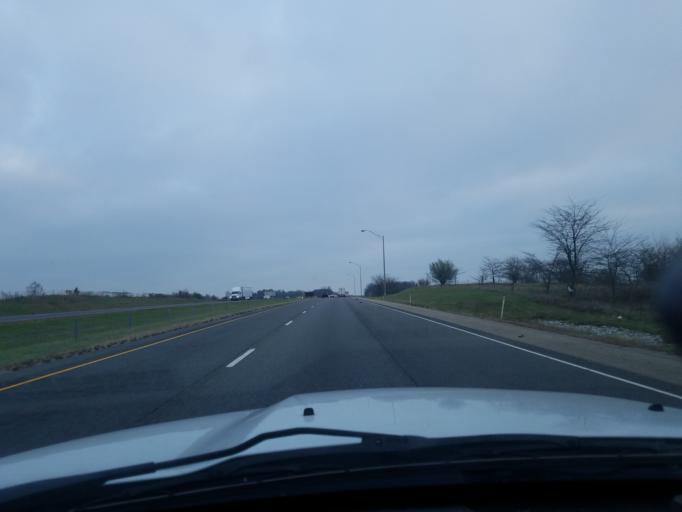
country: US
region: Indiana
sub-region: Delaware County
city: Daleville
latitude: 40.1251
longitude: -85.5686
